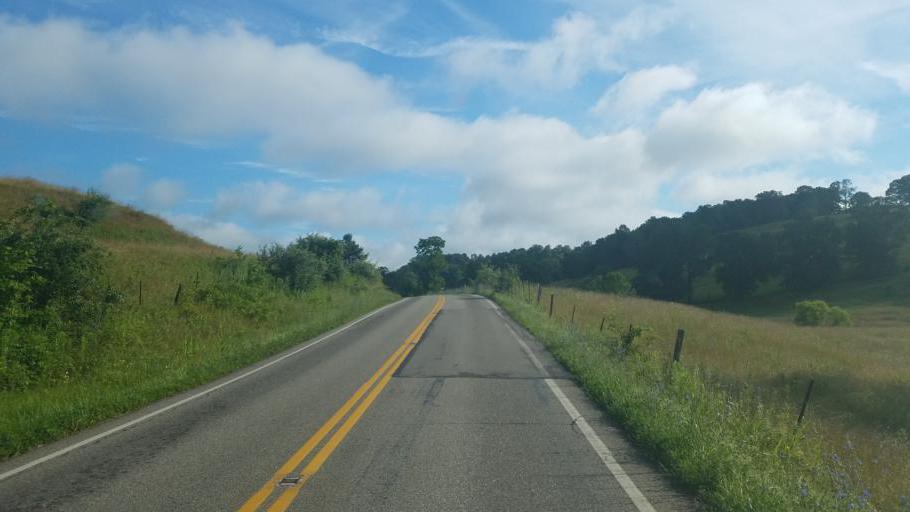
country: US
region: Ohio
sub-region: Gallia County
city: Gallipolis
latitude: 38.7593
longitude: -82.3553
